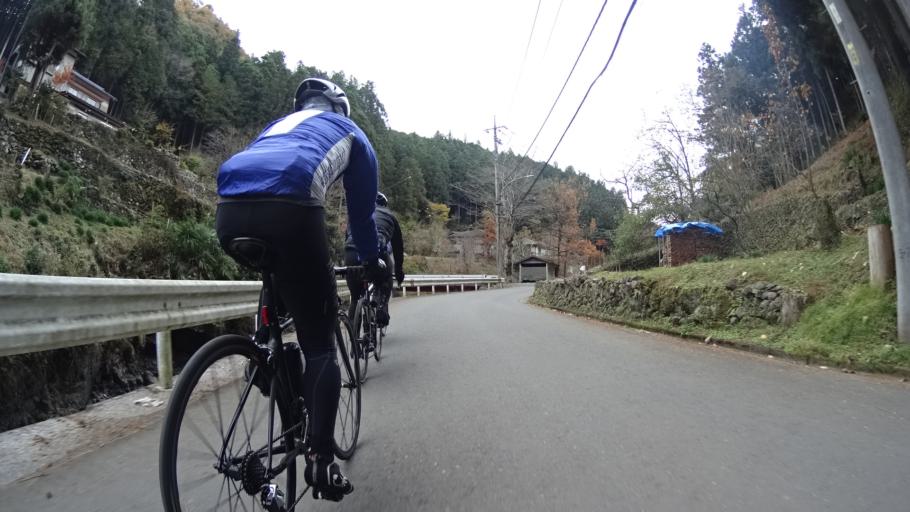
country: JP
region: Saitama
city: Morohongo
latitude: 35.9248
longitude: 139.1897
